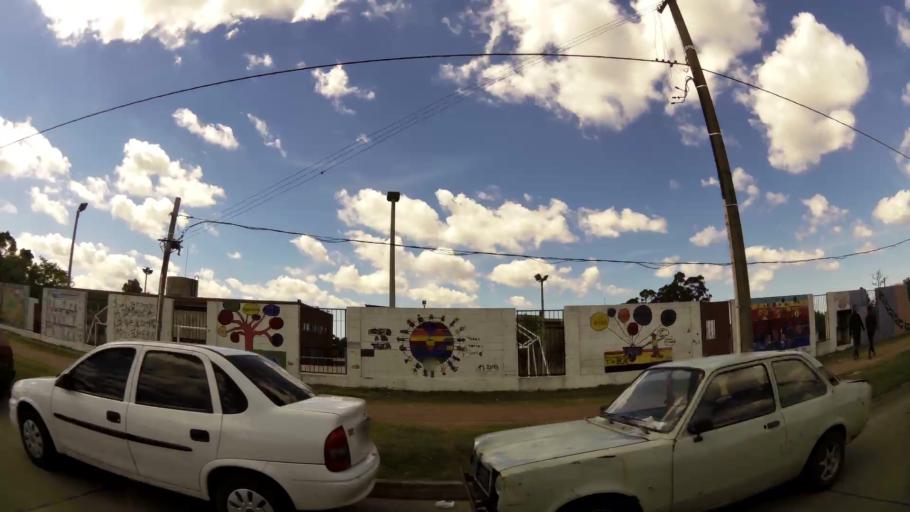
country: UY
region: Canelones
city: Paso de Carrasco
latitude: -34.8388
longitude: -56.1194
